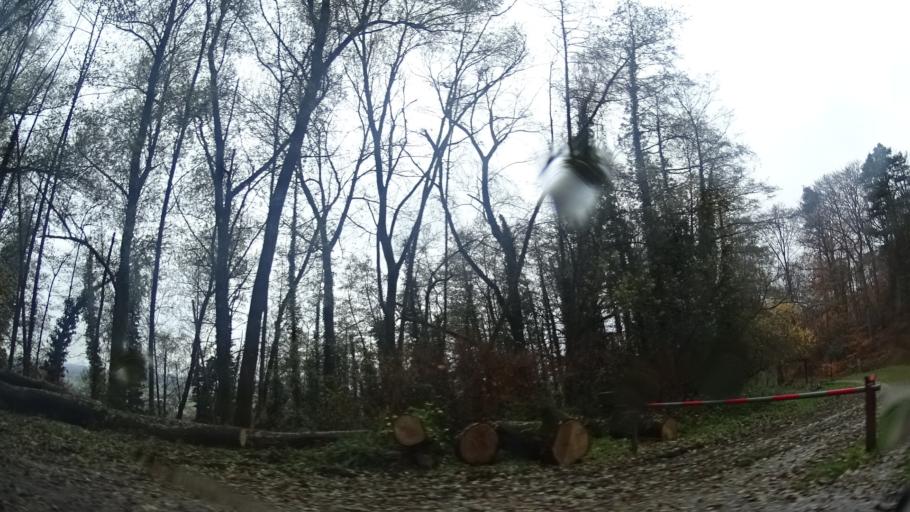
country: DE
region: Baden-Wuerttemberg
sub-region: Karlsruhe Region
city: Sinzheim
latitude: 48.7514
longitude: 8.1831
